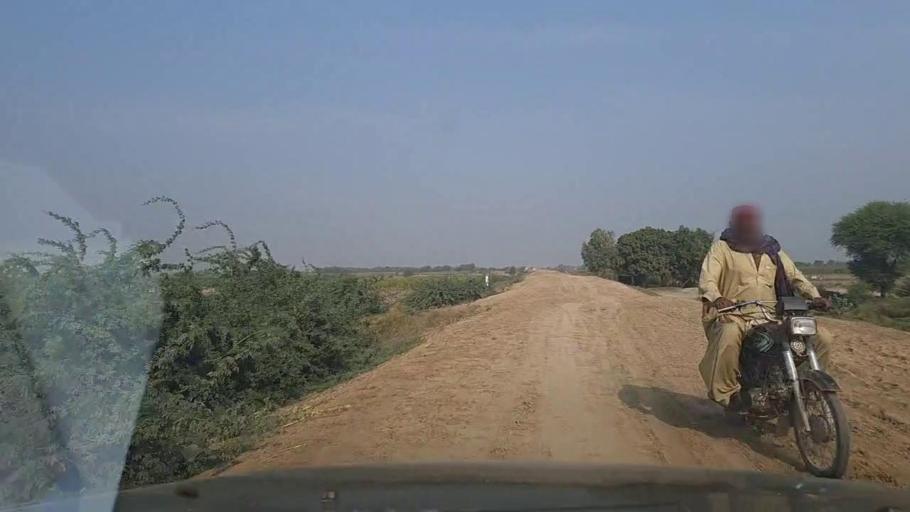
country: PK
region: Sindh
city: Bulri
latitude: 24.9966
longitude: 68.2904
